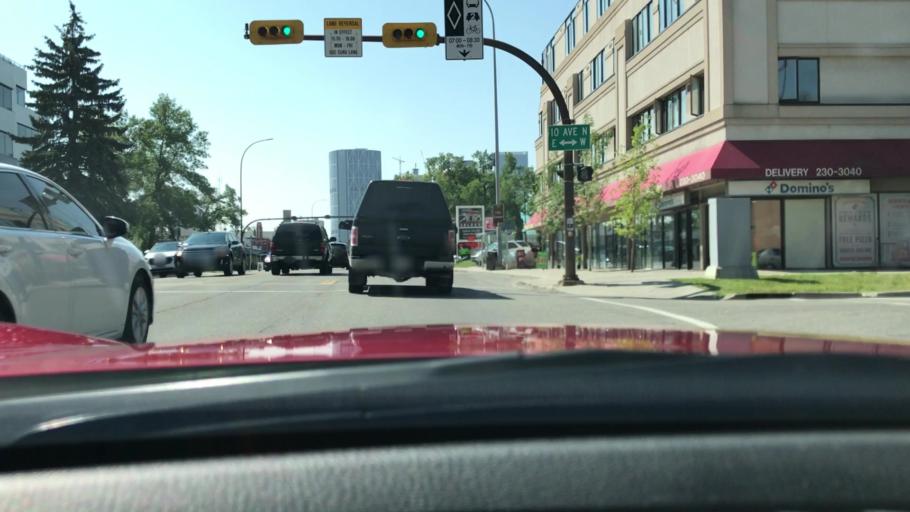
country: CA
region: Alberta
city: Calgary
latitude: 51.0616
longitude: -114.0626
